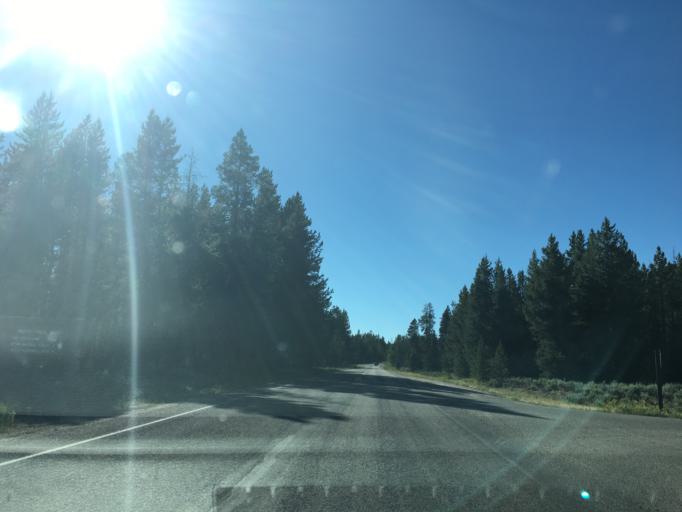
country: US
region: Wyoming
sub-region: Teton County
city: Jackson
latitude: 43.8541
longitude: -110.5201
